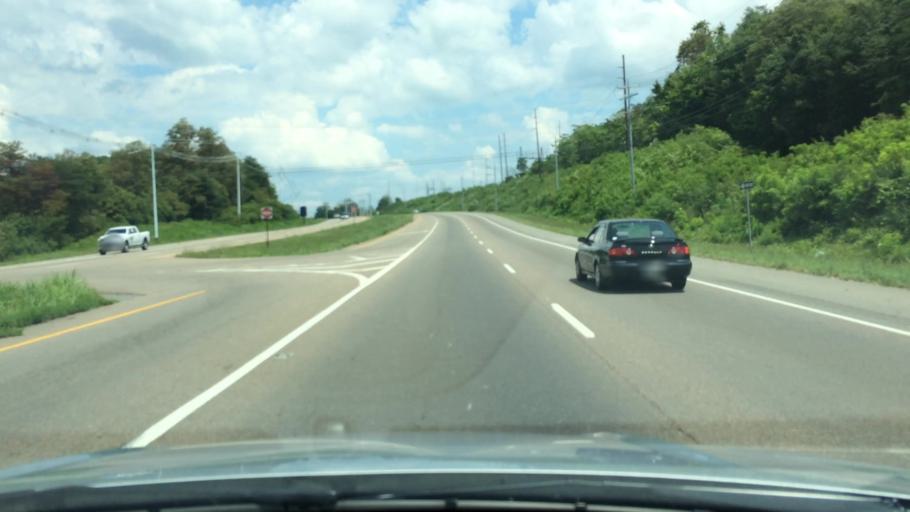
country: US
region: Tennessee
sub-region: Hamblen County
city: Morristown
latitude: 36.1875
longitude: -83.2963
